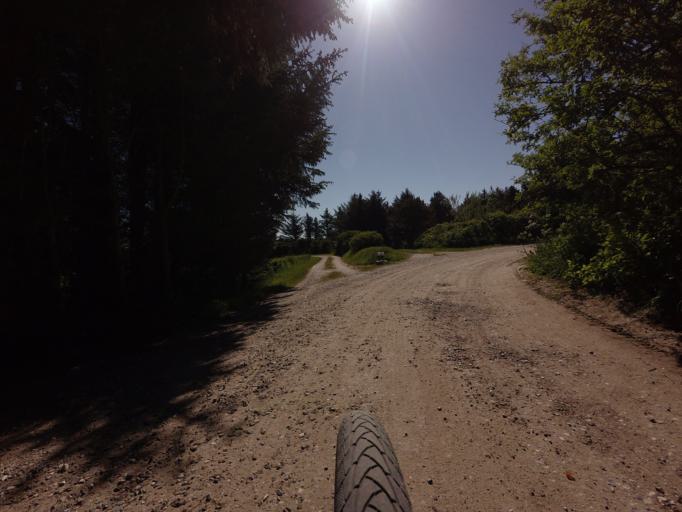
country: DK
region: North Denmark
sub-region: Jammerbugt Kommune
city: Pandrup
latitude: 57.3207
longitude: 9.6695
